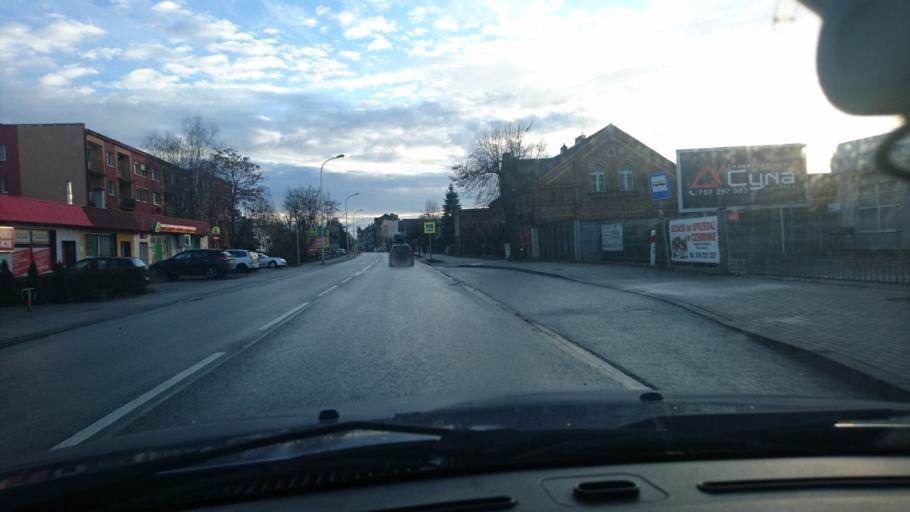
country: PL
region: Greater Poland Voivodeship
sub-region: Powiat kepinski
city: Kepno
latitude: 51.2880
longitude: 17.9932
